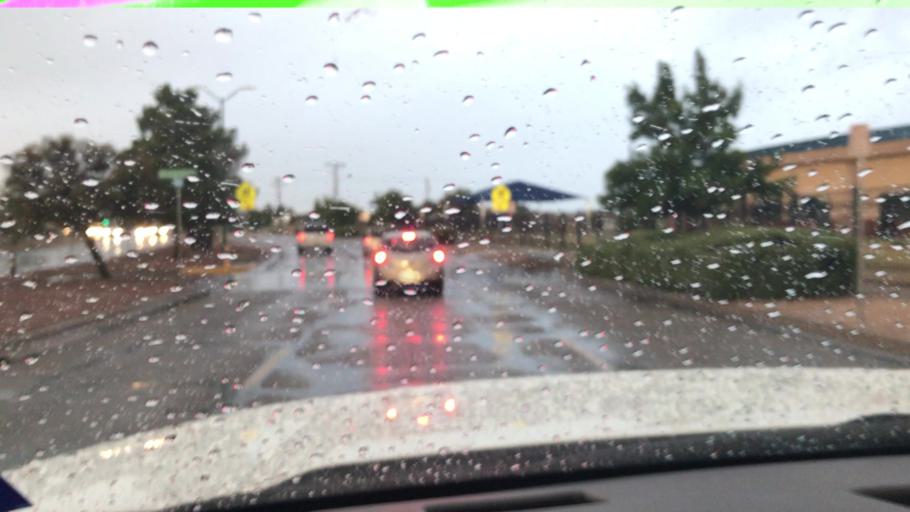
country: US
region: Texas
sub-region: El Paso County
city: Fort Bliss
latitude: 31.7971
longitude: -106.3230
